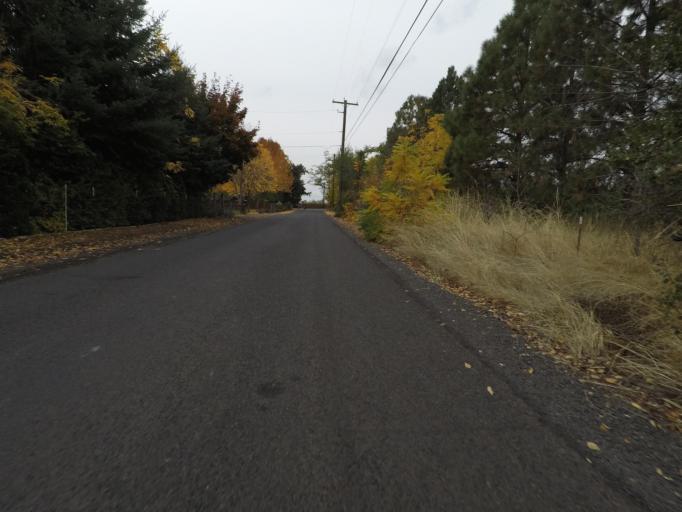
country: US
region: Washington
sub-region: Walla Walla County
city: Walla Walla East
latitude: 46.0749
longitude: -118.2820
